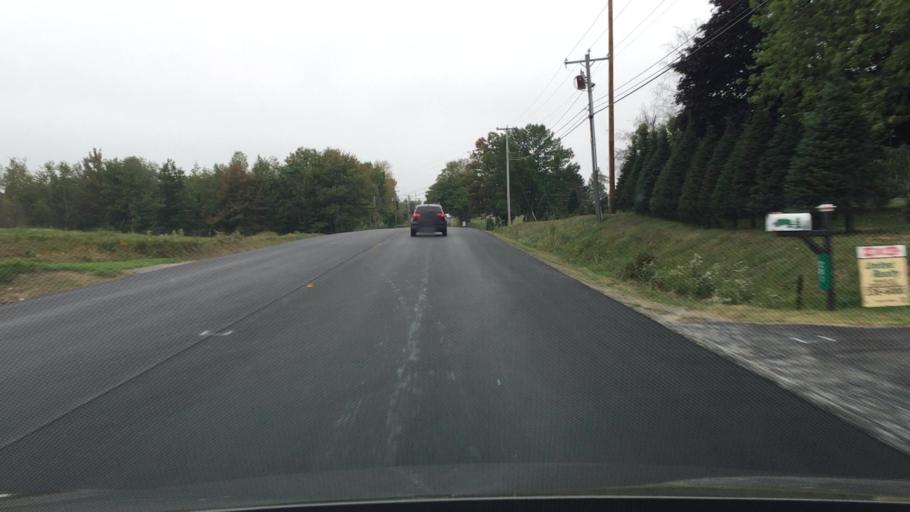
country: US
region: Maine
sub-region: Waldo County
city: Belfast
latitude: 44.4113
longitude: -69.0725
